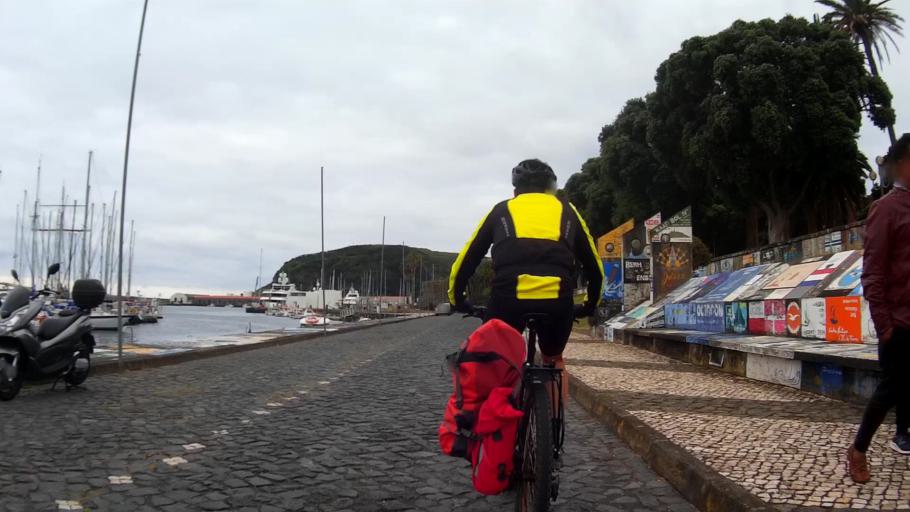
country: PT
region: Azores
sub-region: Horta
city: Horta
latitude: 38.5331
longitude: -28.6261
